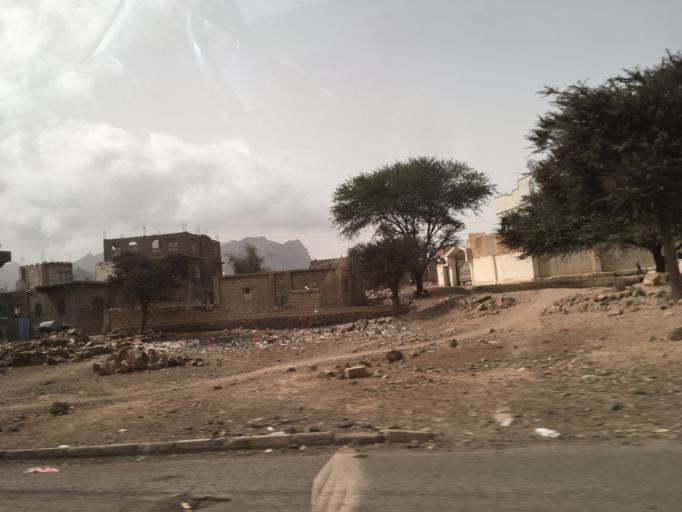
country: YE
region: Ad Dali'
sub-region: Ad Dhale'e
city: Dhalie
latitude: 13.6970
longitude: 44.7319
